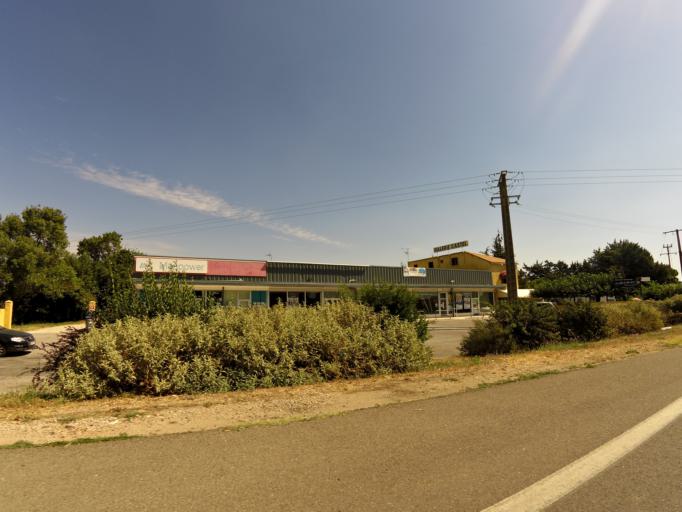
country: FR
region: Languedoc-Roussillon
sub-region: Departement de l'Herault
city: Lunel-Viel
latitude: 43.6805
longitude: 4.0991
